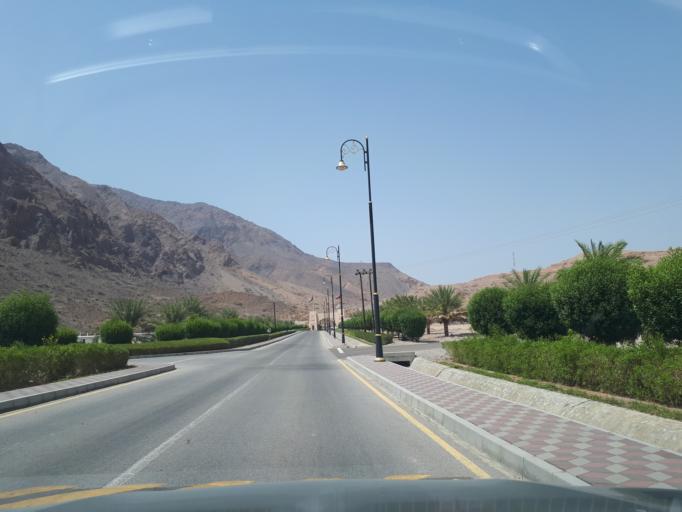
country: OM
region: Ash Sharqiyah
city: Ibra'
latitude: 23.0920
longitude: 58.8506
